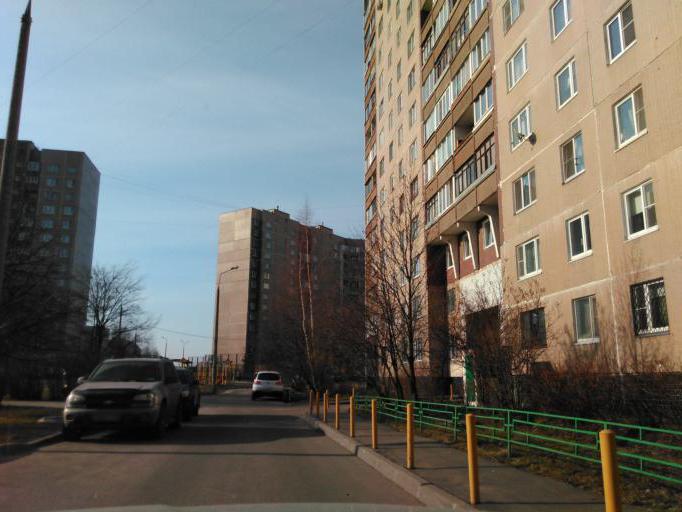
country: RU
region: Moskovskaya
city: Andreyevka
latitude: 55.9724
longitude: 37.1513
